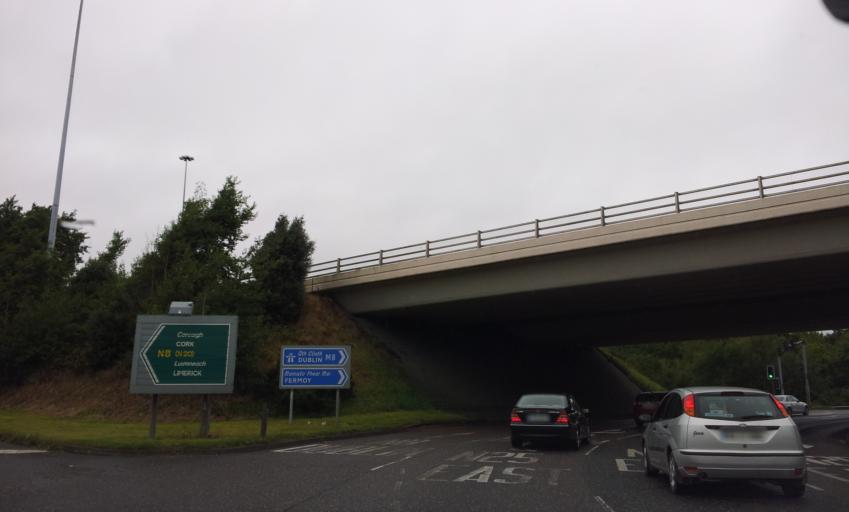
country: IE
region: Munster
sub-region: County Cork
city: Passage West
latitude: 51.9041
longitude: -8.3885
